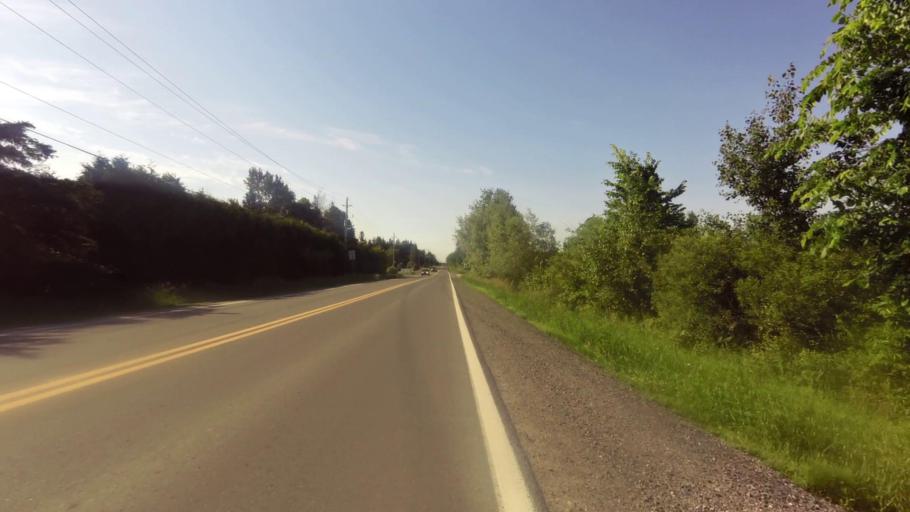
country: CA
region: Ontario
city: Ottawa
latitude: 45.2580
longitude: -75.5681
